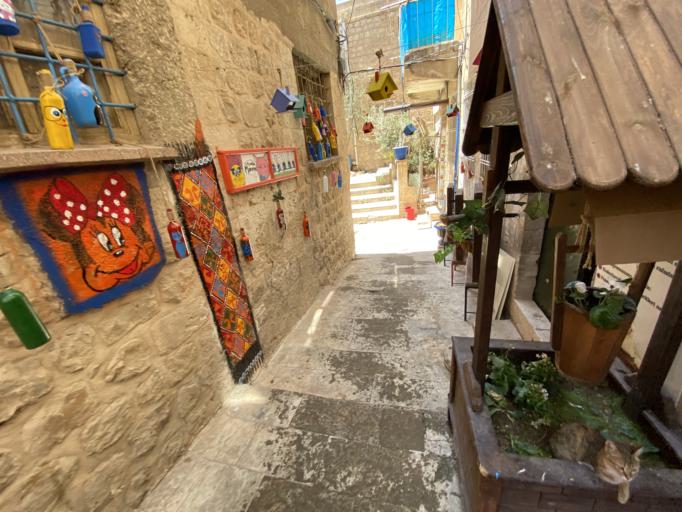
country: TR
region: Mardin
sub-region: Mardin Ilcesi
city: Mardin
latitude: 37.3147
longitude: 40.7437
